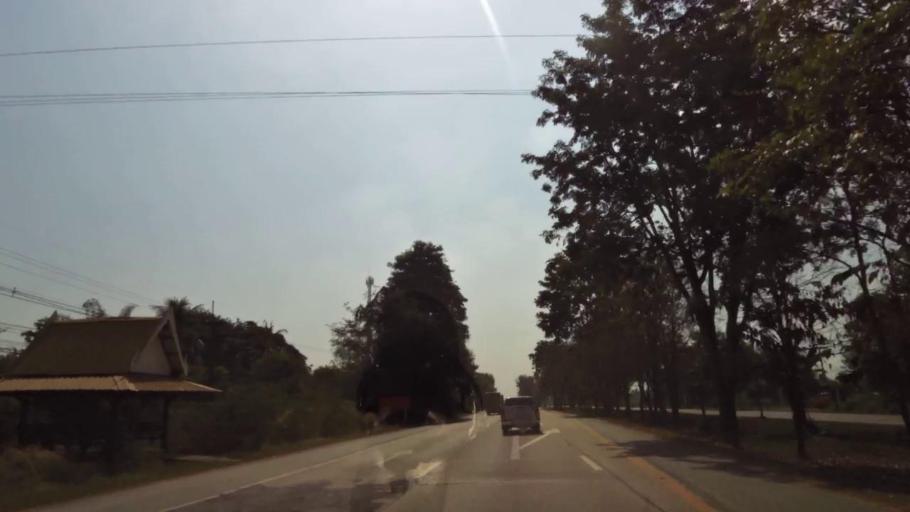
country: TH
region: Phichit
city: Wachira Barami
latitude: 16.5330
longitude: 100.1436
